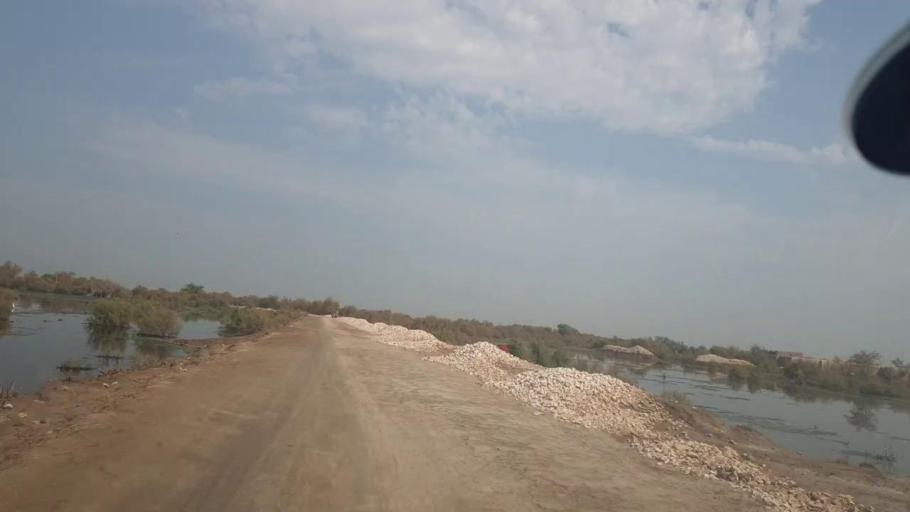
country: PK
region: Balochistan
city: Mehrabpur
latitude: 28.0924
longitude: 68.0955
